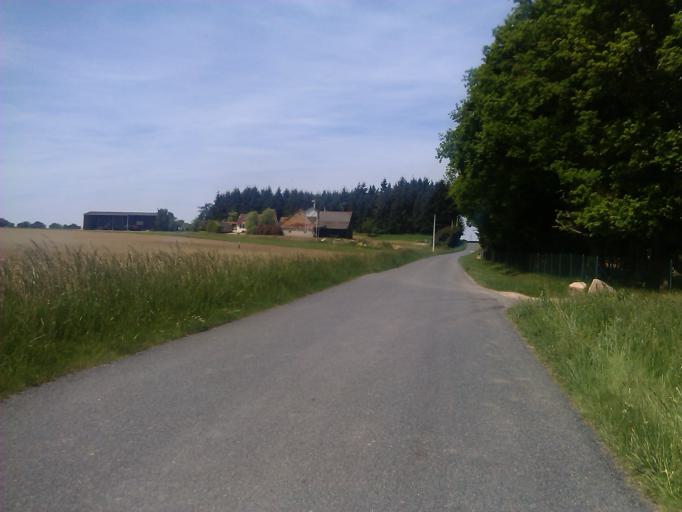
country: FR
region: Centre
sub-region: Departement du Cher
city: Le Chatelet
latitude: 46.5817
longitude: 2.3847
